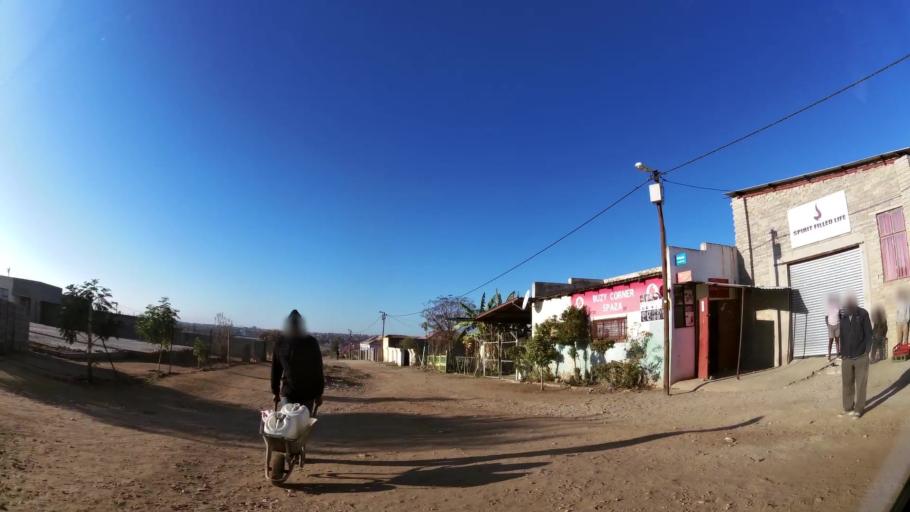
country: ZA
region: Limpopo
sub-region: Capricorn District Municipality
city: Polokwane
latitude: -23.8396
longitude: 29.3631
